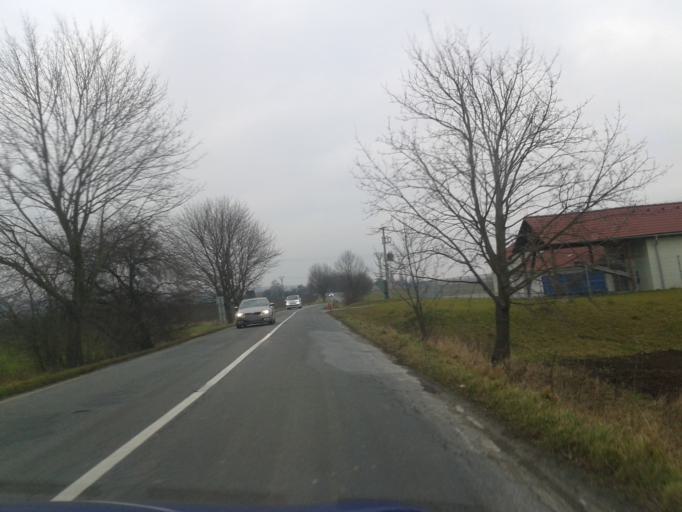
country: CZ
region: Olomoucky
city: Drahanovice
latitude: 49.5787
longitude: 17.0911
